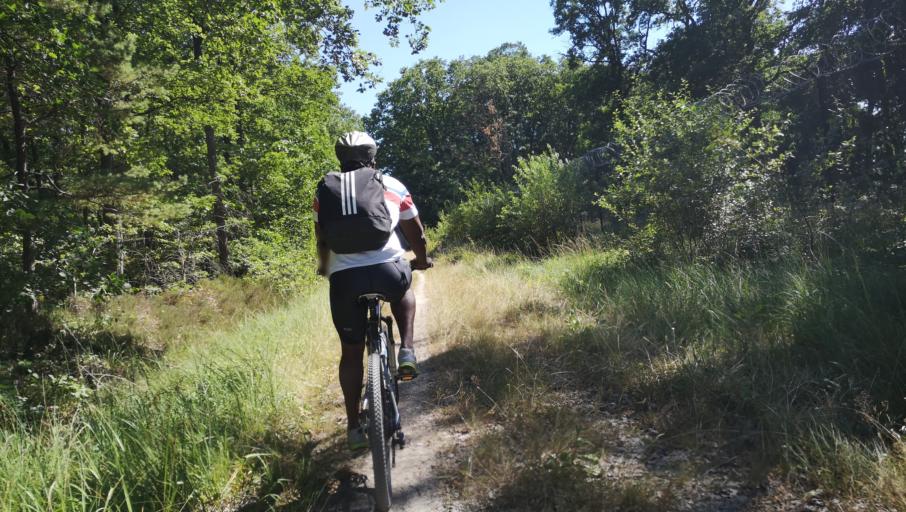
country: FR
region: Centre
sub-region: Departement du Loiret
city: Semoy
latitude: 47.9559
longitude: 1.9447
